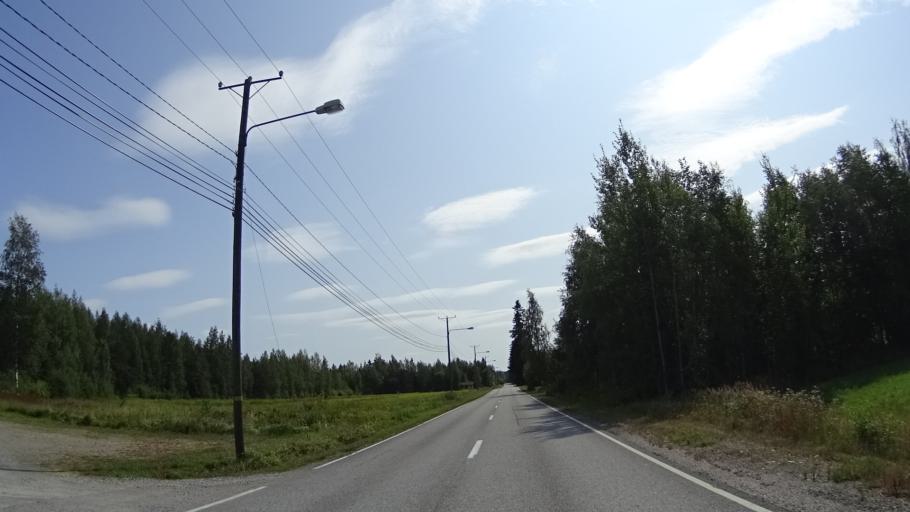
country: FI
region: Pirkanmaa
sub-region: Ylae-Pirkanmaa
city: Maenttae
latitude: 61.9162
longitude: 24.7740
